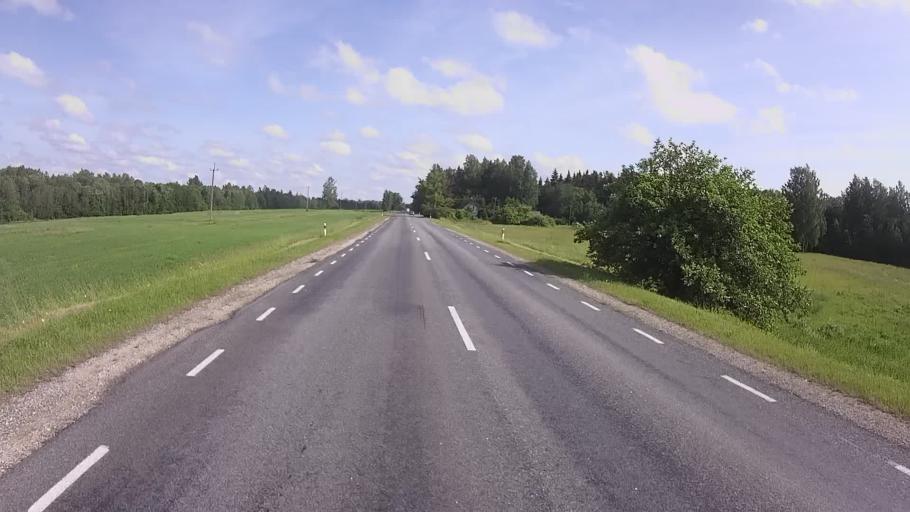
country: EE
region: Tartu
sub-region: Elva linn
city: Elva
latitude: 57.9780
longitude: 26.2609
